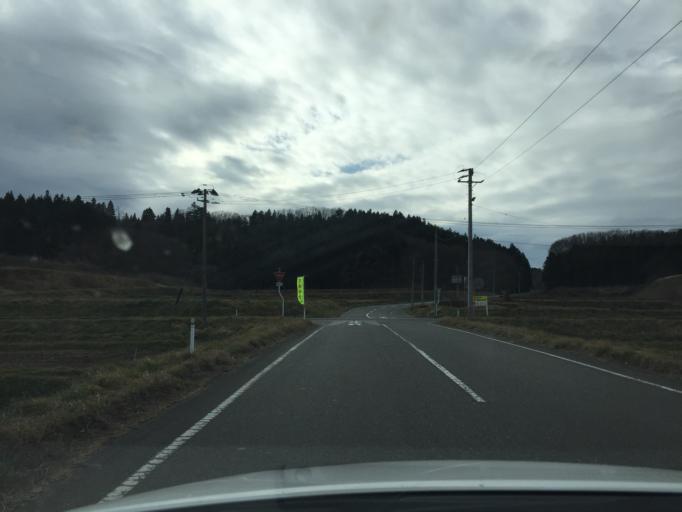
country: JP
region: Fukushima
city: Funehikimachi-funehiki
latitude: 37.3037
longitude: 140.6060
